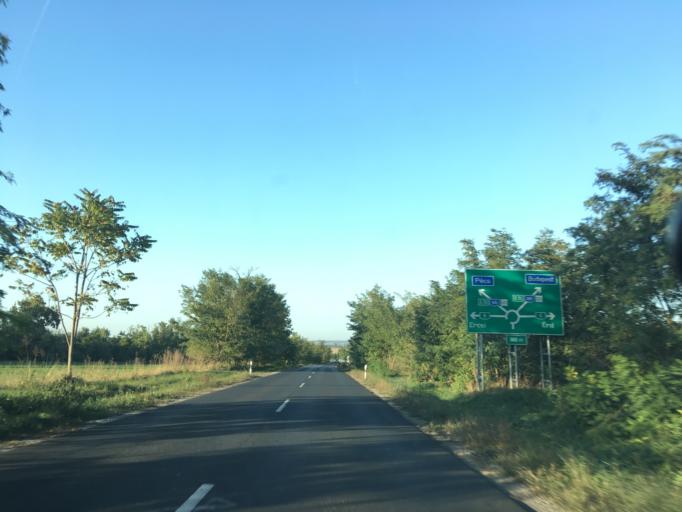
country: HU
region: Pest
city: Szazhalombatta
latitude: 47.3329
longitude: 18.8945
